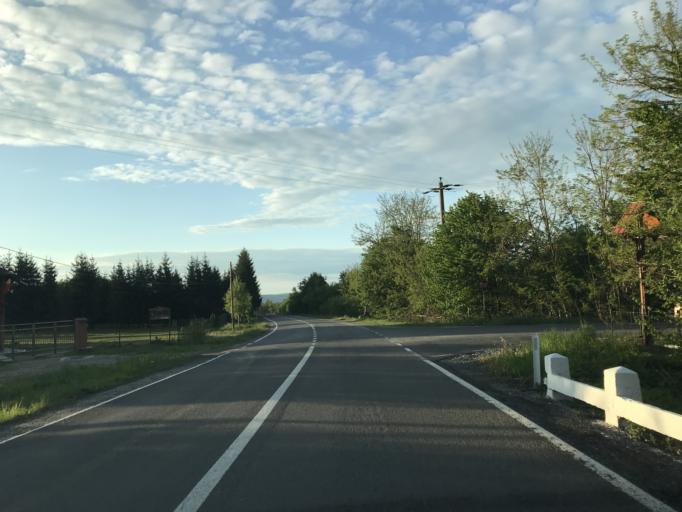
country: RO
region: Sibiu
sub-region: Comuna Cartisoara
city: Cartisoara
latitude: 45.6933
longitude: 24.5725
